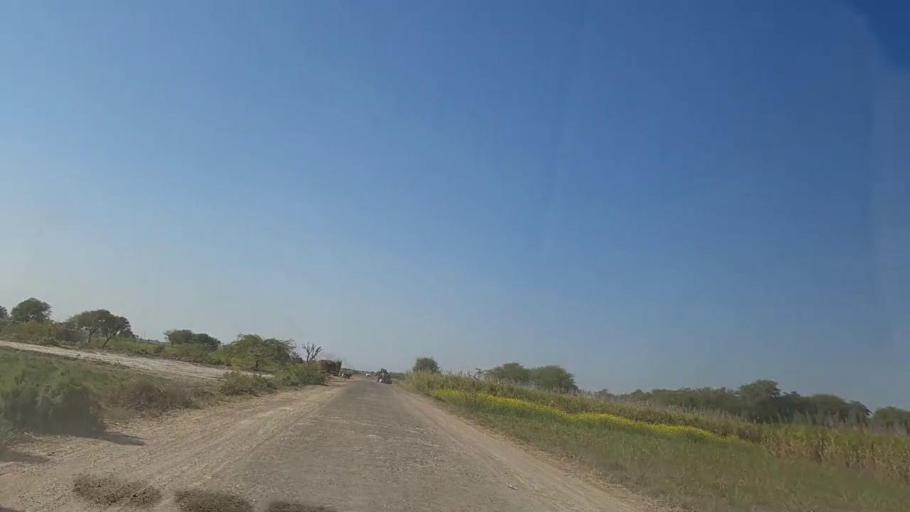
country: PK
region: Sindh
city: Digri
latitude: 25.1416
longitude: 69.0156
